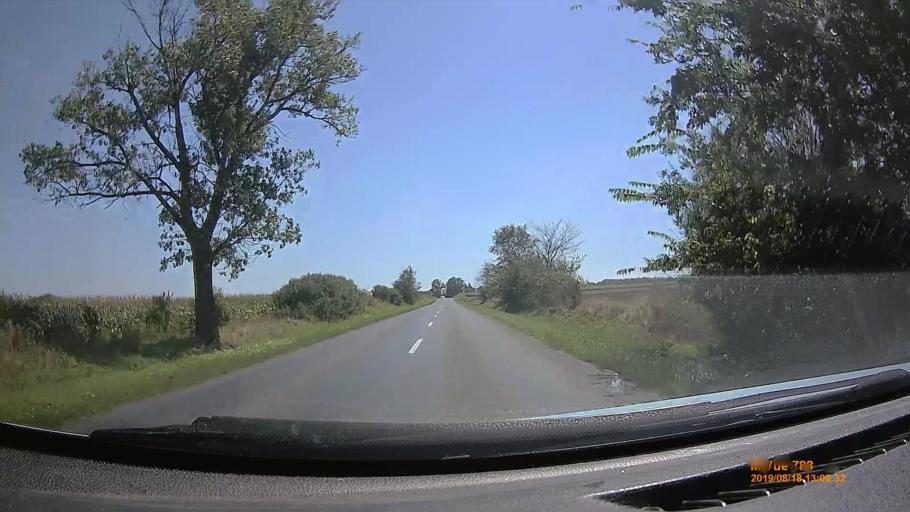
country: HU
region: Fejer
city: Kaloz
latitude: 46.9258
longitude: 18.5110
